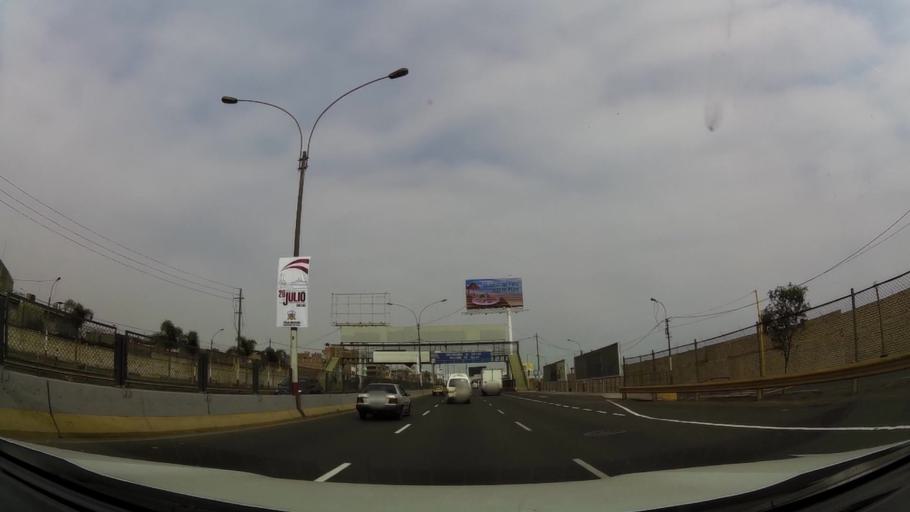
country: PE
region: Callao
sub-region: Callao
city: Callao
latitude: -12.0323
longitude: -77.1008
